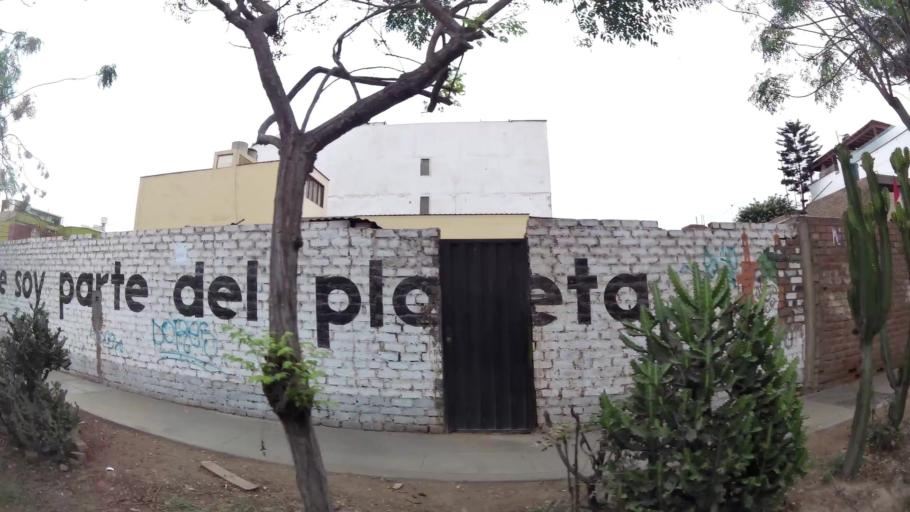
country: PE
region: Lima
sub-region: Lima
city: Surco
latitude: -12.1417
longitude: -76.9995
